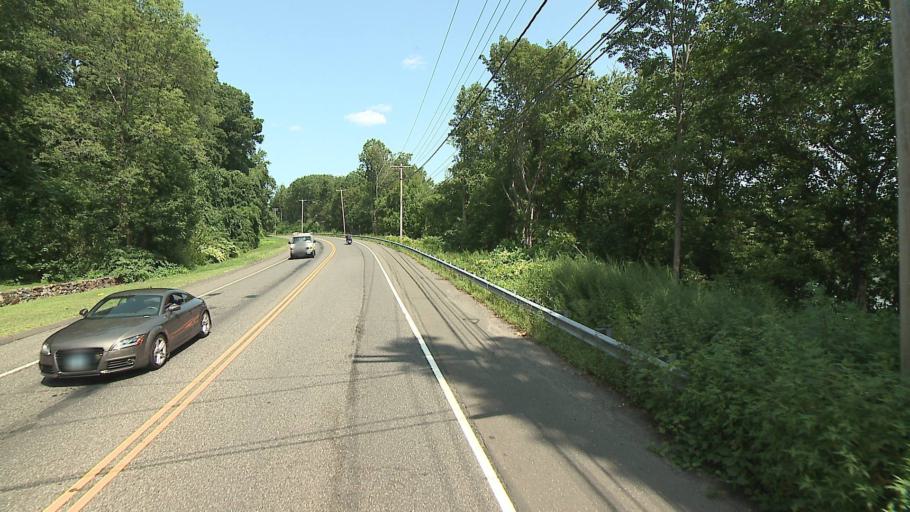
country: US
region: Connecticut
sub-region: Fairfield County
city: Shelton
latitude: 41.2740
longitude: -73.0895
